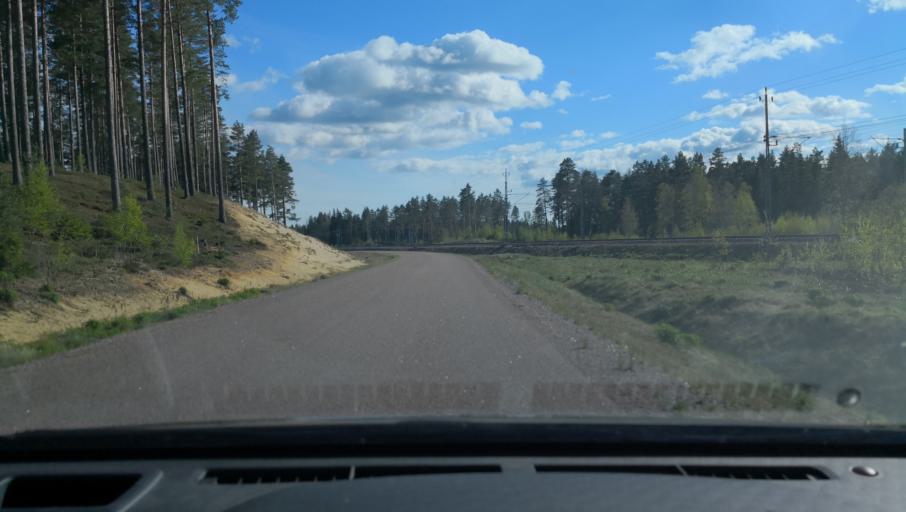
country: SE
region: OErebro
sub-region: Askersunds Kommun
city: Asbro
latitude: 58.9457
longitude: 15.0414
